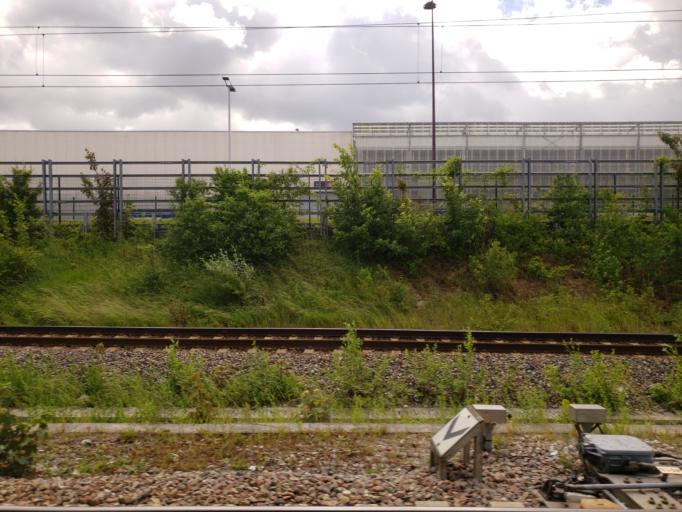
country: FR
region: Ile-de-France
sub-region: Departement de Seine-Saint-Denis
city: Villepinte
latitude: 48.9718
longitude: 2.5132
